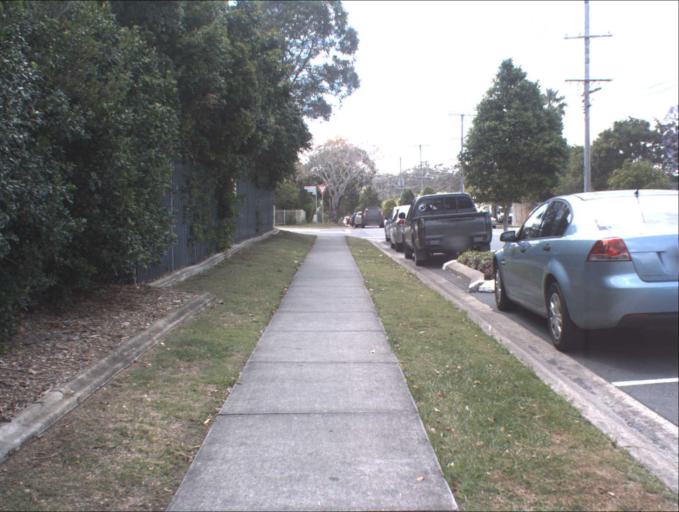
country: AU
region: Queensland
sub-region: Logan
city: Logan City
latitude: -27.6568
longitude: 153.1202
